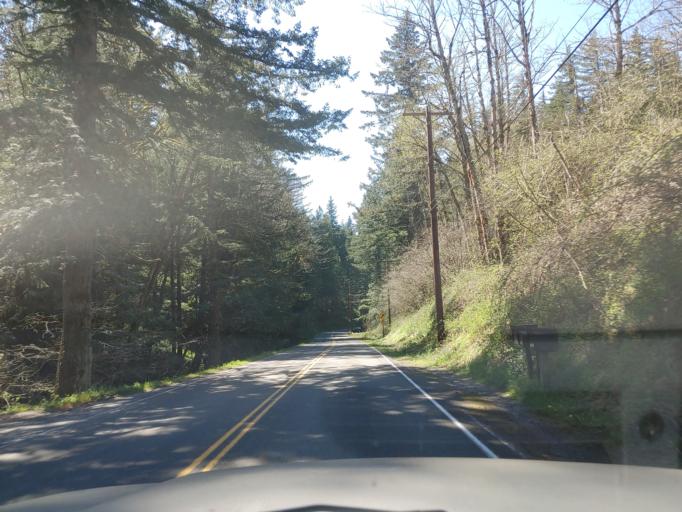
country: US
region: Oregon
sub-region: Multnomah County
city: Troutdale
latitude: 45.5214
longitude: -122.3218
